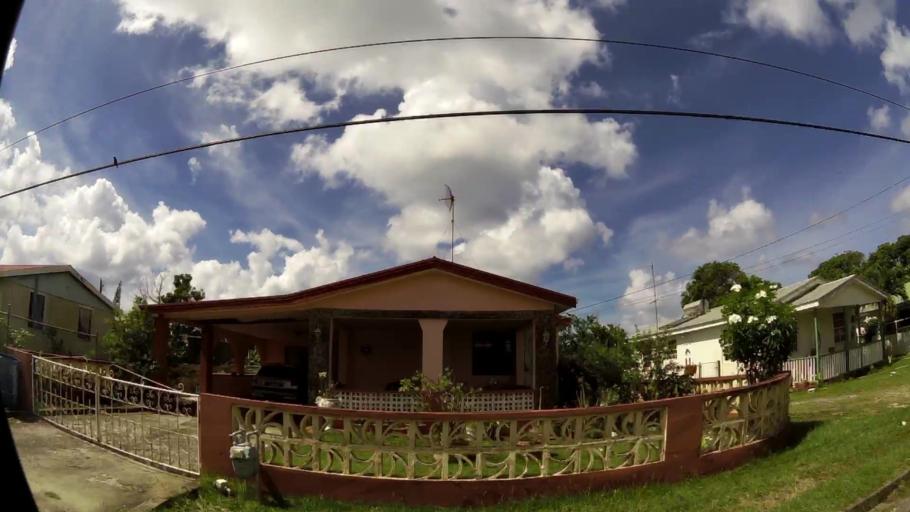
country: BB
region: Saint James
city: Holetown
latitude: 13.1500
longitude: -59.6293
